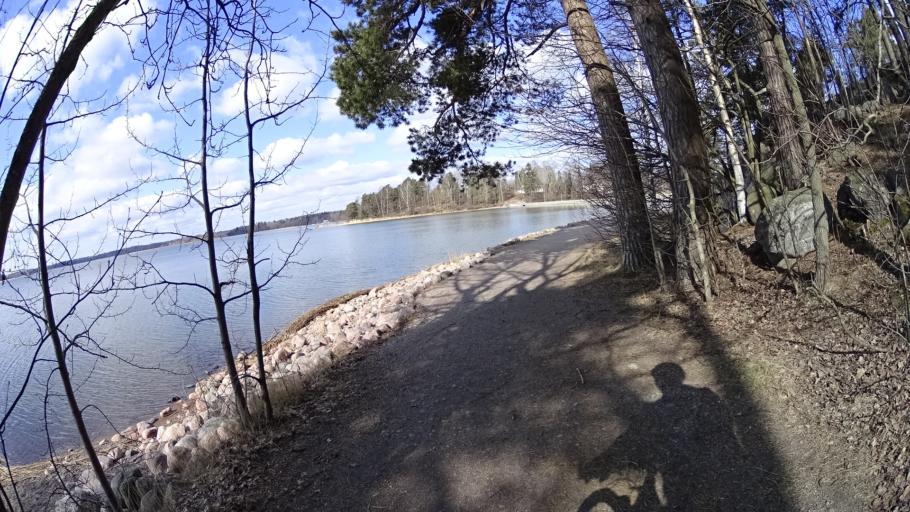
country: FI
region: Uusimaa
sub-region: Helsinki
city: Teekkarikylae
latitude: 60.2018
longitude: 24.8542
